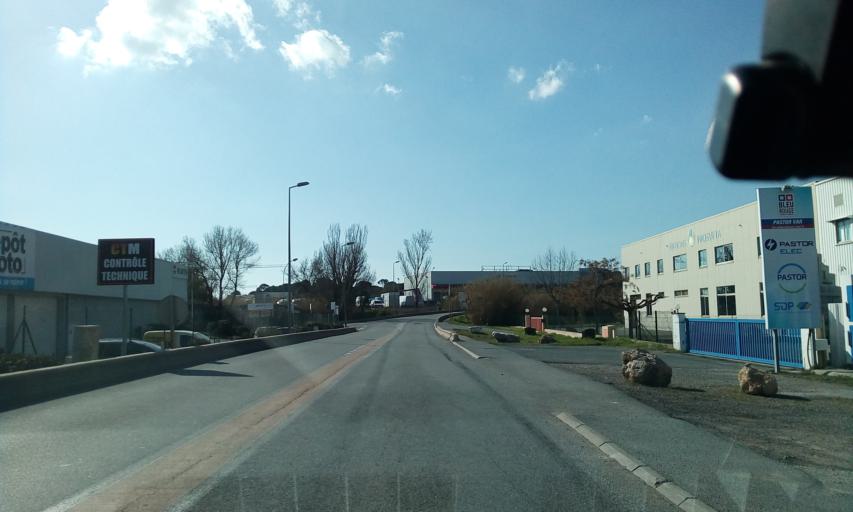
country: FR
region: Provence-Alpes-Cote d'Azur
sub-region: Departement du Var
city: Frejus
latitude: 43.4691
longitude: 6.7344
